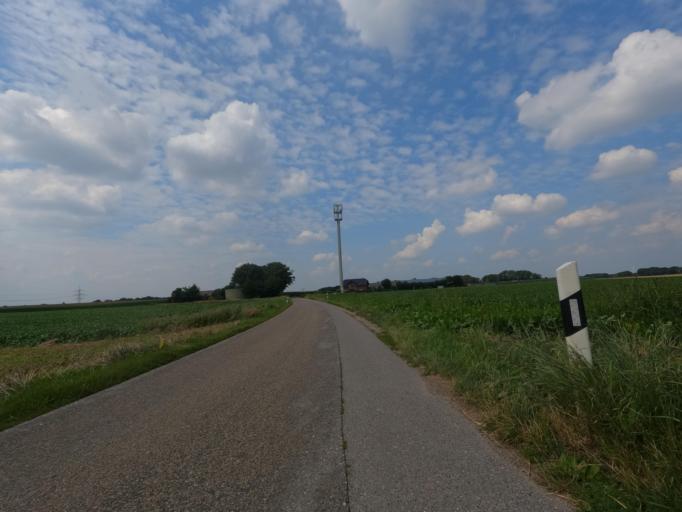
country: DE
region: North Rhine-Westphalia
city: Geilenkirchen
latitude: 50.9700
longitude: 6.1597
